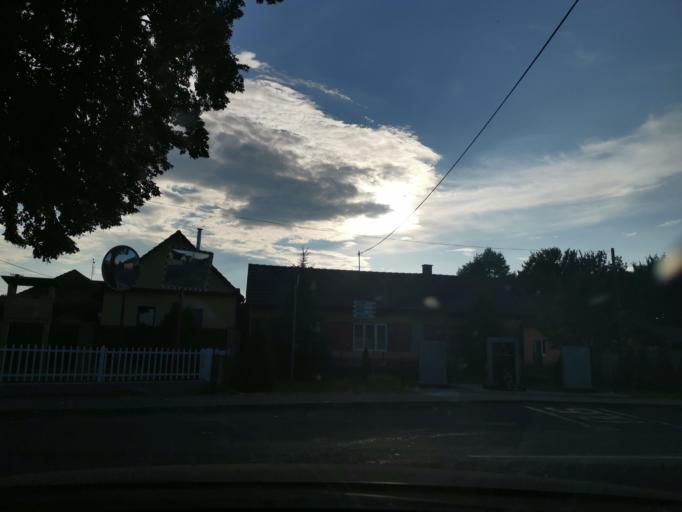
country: SK
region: Trnavsky
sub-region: Okres Senica
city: Senica
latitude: 48.6554
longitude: 17.2664
